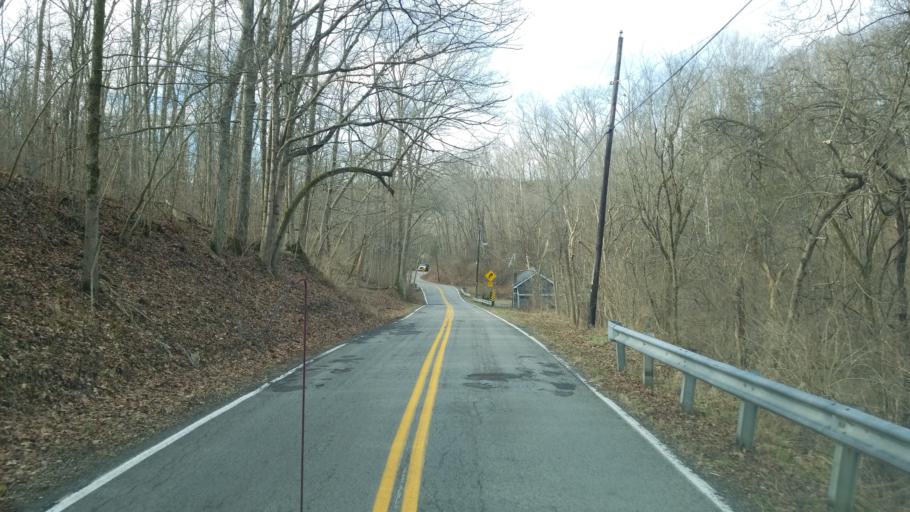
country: US
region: Ohio
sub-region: Warren County
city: Waynesville
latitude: 39.4503
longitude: -84.0928
